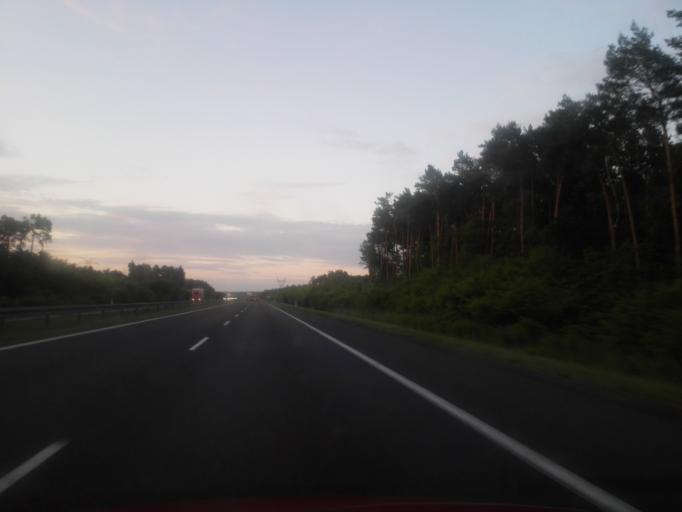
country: PL
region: Lodz Voivodeship
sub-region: Powiat radomszczanski
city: Radomsko
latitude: 51.0406
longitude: 19.3440
